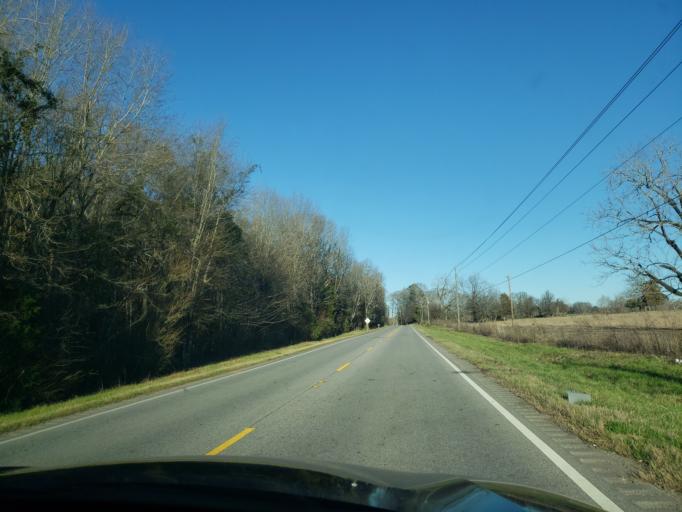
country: US
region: Alabama
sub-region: Lee County
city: Auburn
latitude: 32.6024
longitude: -85.5855
